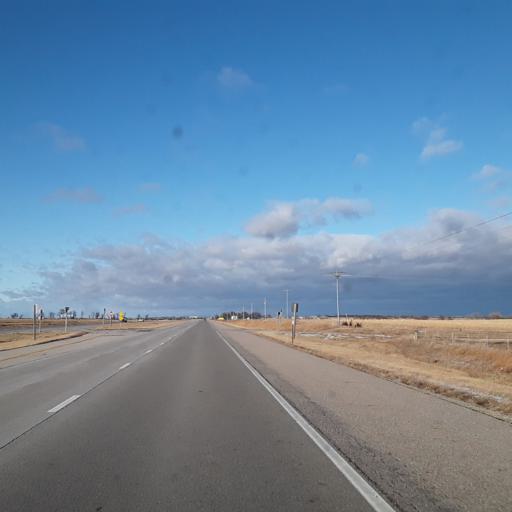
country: US
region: Kansas
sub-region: Republic County
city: Belleville
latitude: 39.9126
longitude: -97.6143
